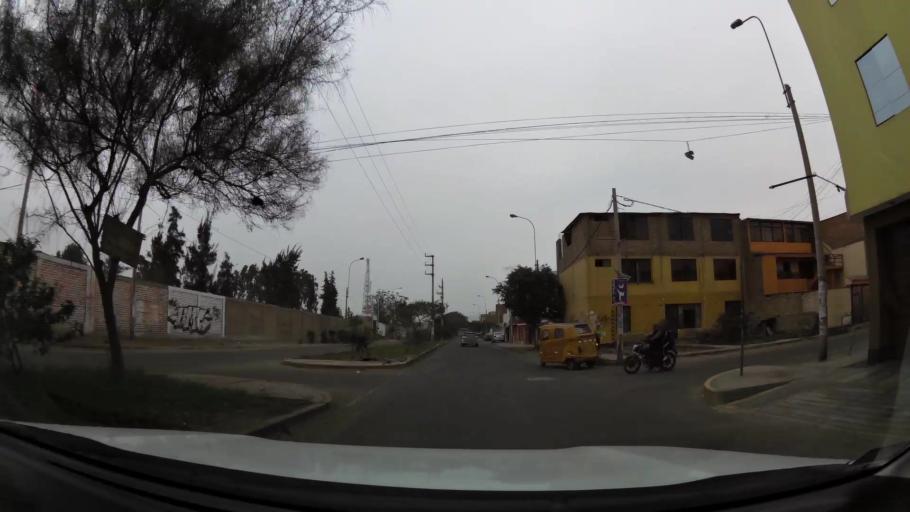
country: PE
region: Lima
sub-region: Lima
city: Surco
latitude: -12.1712
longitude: -76.9740
